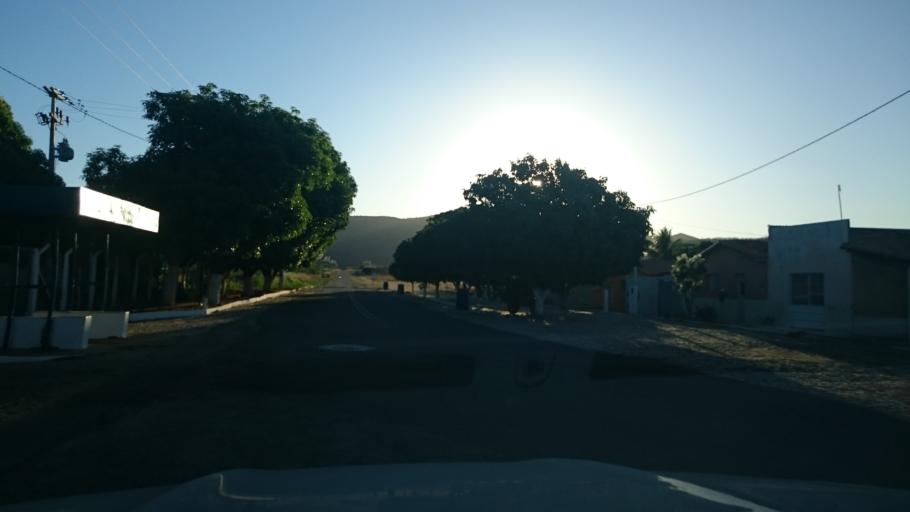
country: BR
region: Rio Grande do Norte
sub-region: Umarizal
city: Umarizal
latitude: -5.9938
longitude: -37.9485
